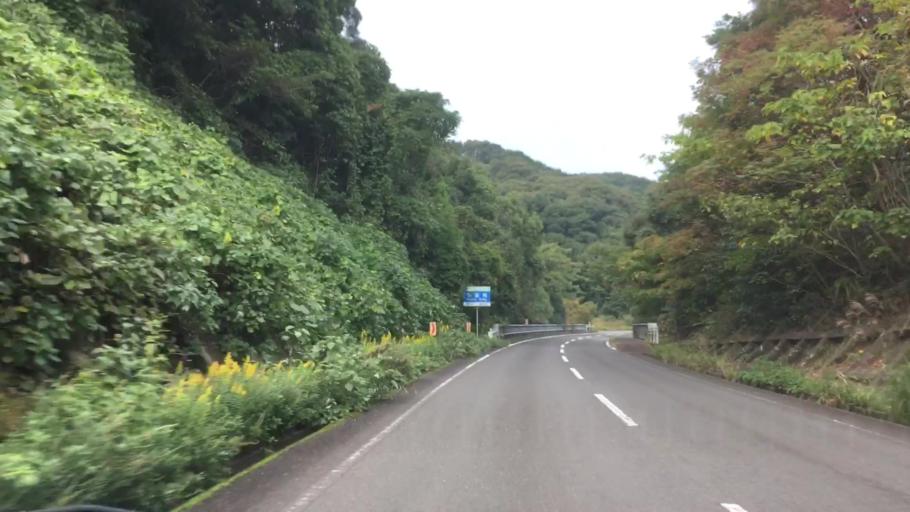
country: JP
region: Nagasaki
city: Sasebo
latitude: 32.9971
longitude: 129.7097
